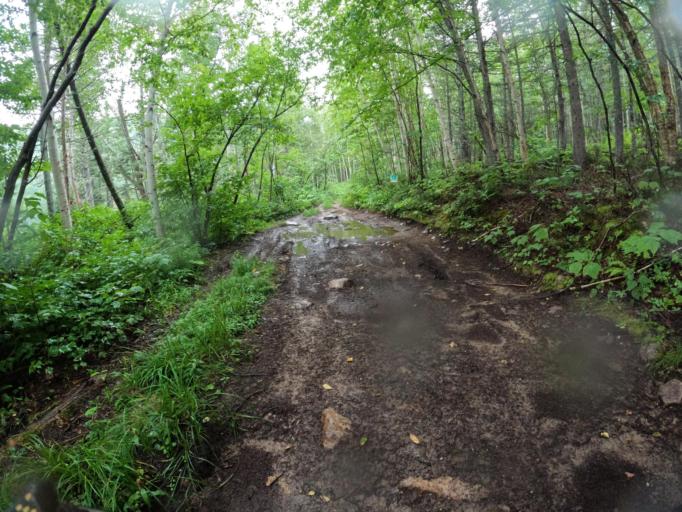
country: CA
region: Quebec
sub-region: Capitale-Nationale
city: La Malbaie
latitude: 47.8346
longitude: -70.4612
